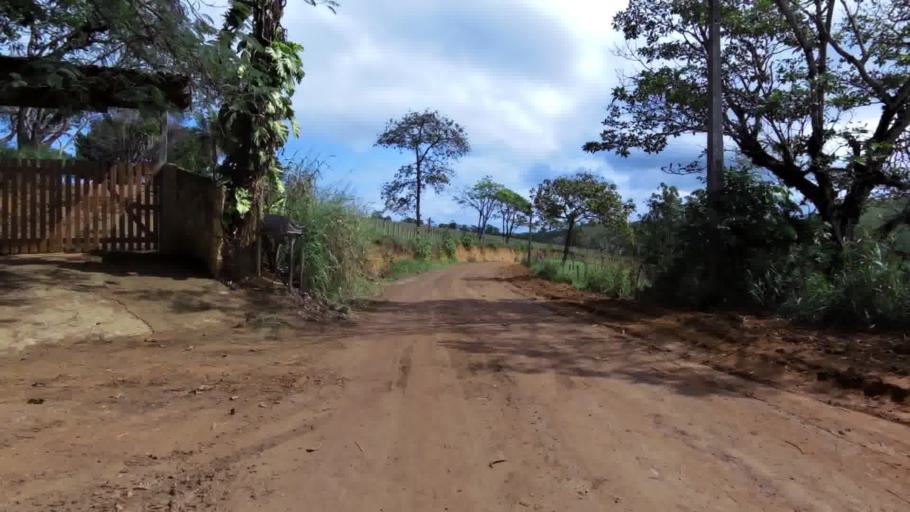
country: BR
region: Espirito Santo
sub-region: Piuma
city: Piuma
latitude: -20.8115
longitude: -40.6679
